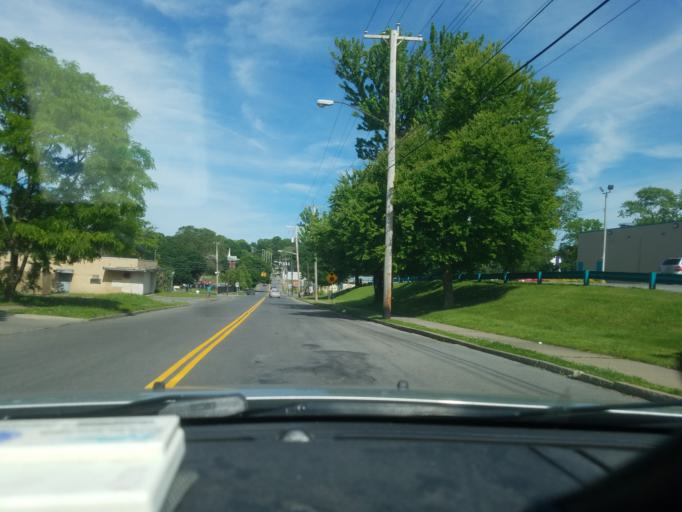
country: US
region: New York
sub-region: Onondaga County
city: Syracuse
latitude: 43.0482
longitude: -76.1161
